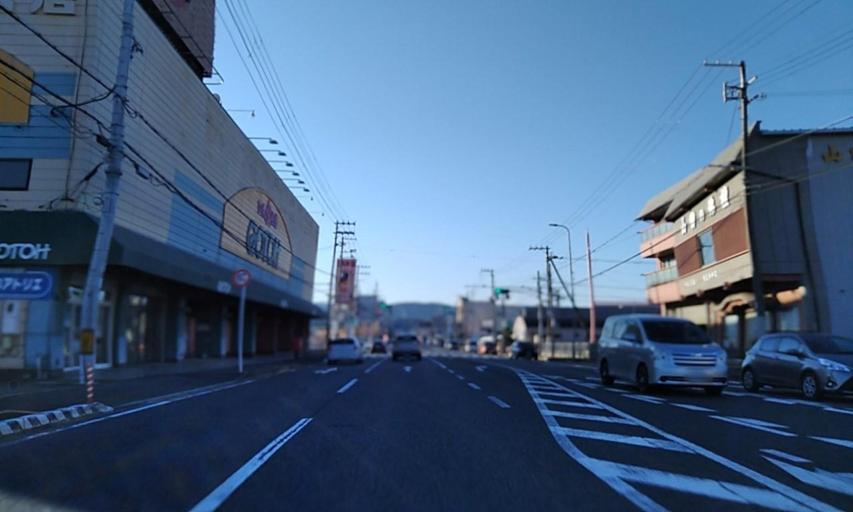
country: JP
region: Wakayama
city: Kainan
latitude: 34.1830
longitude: 135.1860
